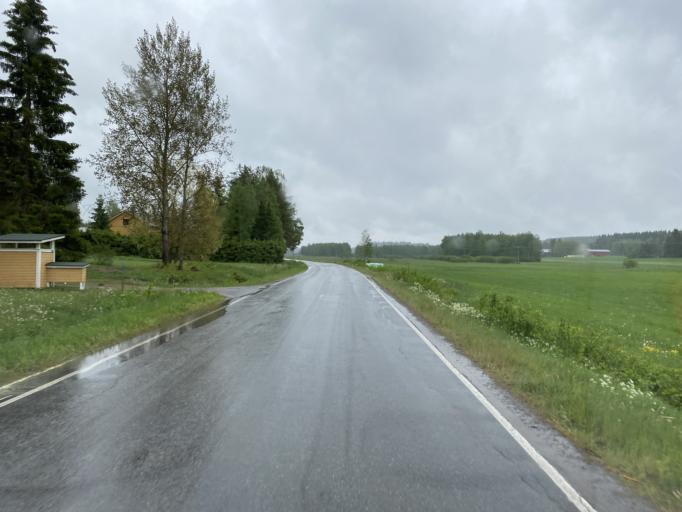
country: FI
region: Haeme
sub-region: Forssa
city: Humppila
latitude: 61.0421
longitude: 23.3957
